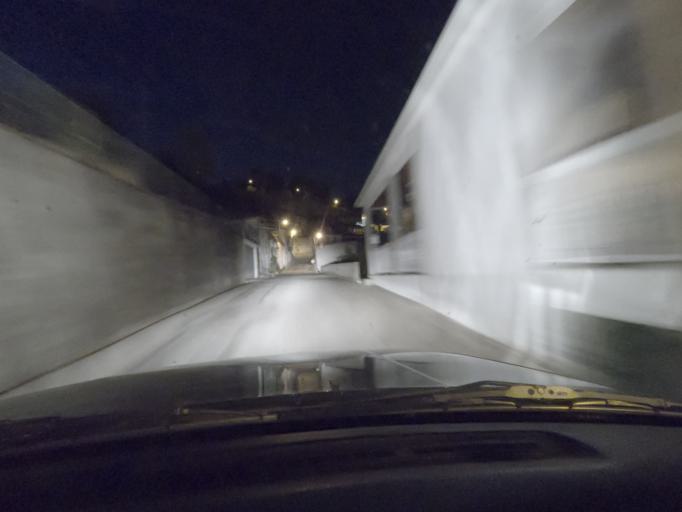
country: PT
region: Vila Real
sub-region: Santa Marta de Penaguiao
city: Santa Marta de Penaguiao
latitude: 41.2226
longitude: -7.8393
